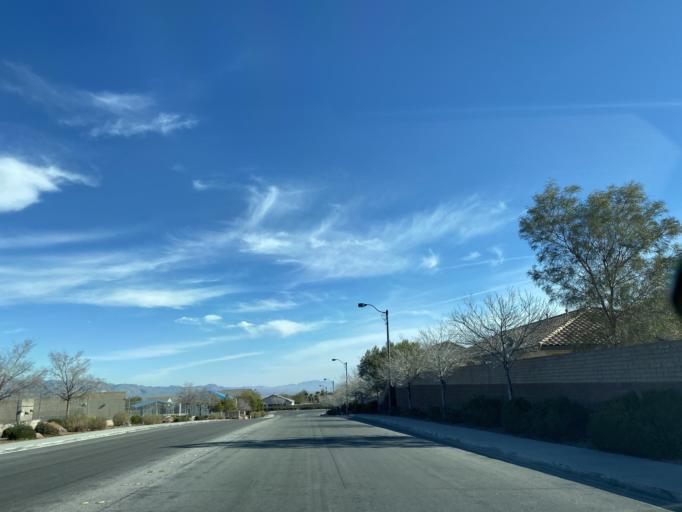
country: US
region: Nevada
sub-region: Clark County
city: Summerlin South
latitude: 36.2956
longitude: -115.3217
